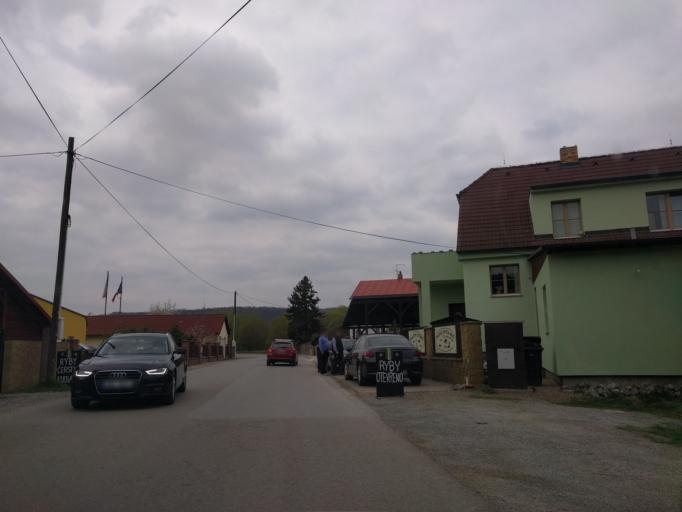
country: CZ
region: Central Bohemia
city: Revnice
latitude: 49.9172
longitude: 14.2491
